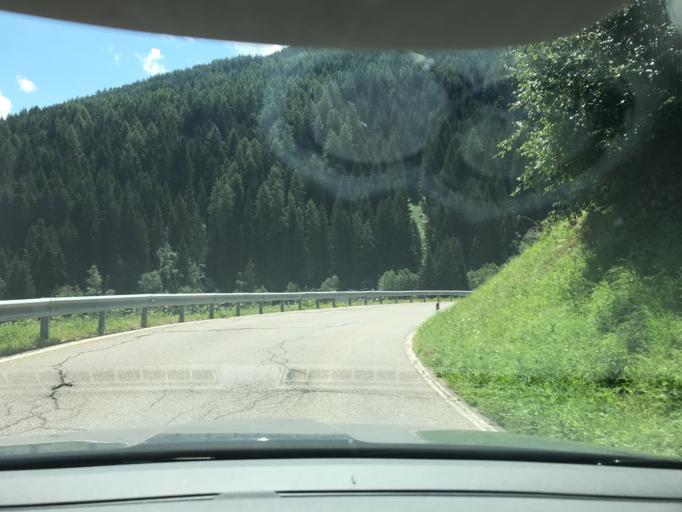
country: IT
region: Trentino-Alto Adige
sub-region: Bolzano
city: Valdaora di Mezzo
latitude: 46.7496
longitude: 12.0109
